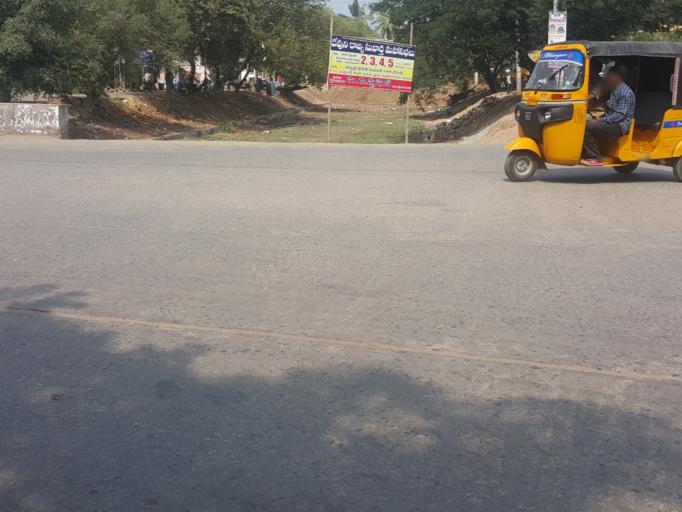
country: IN
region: Andhra Pradesh
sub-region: Guntur
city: Mangalagiri
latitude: 16.2430
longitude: 80.6495
